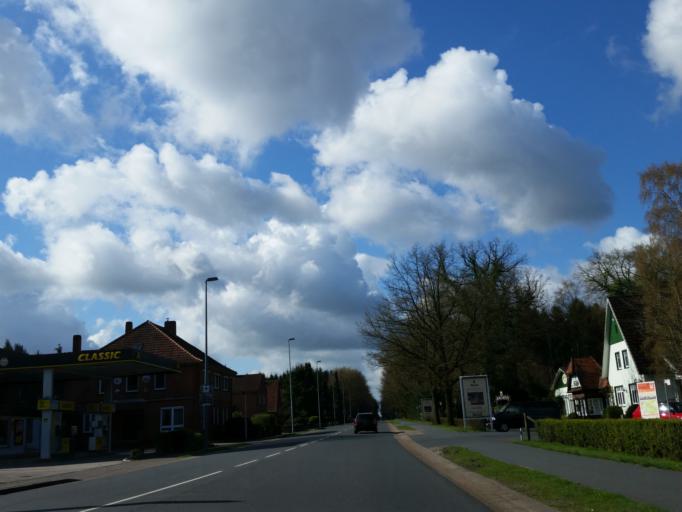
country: DE
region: Lower Saxony
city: Ahausen
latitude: 53.0773
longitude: 9.3553
